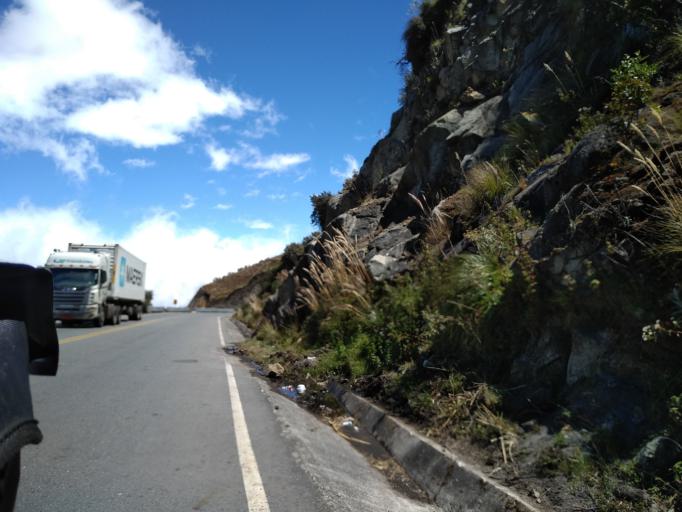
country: EC
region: Cotopaxi
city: Pujili
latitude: -0.9903
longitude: -78.9541
